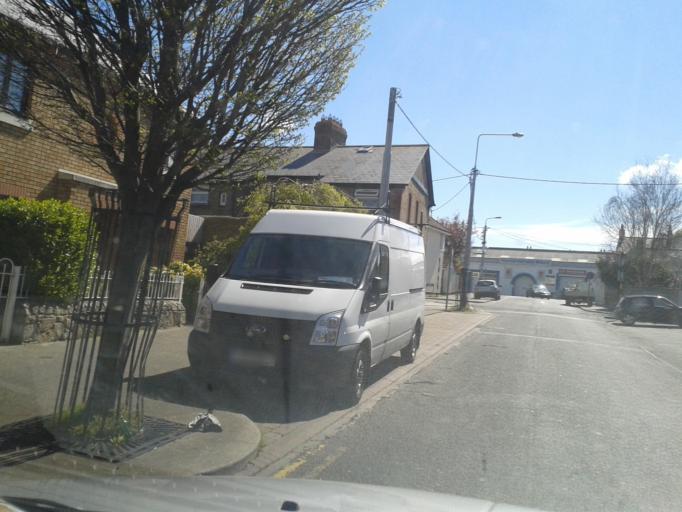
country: IE
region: Leinster
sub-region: Dun Laoghaire-Rathdown
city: Dun Laoghaire
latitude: 53.2921
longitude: -6.1407
